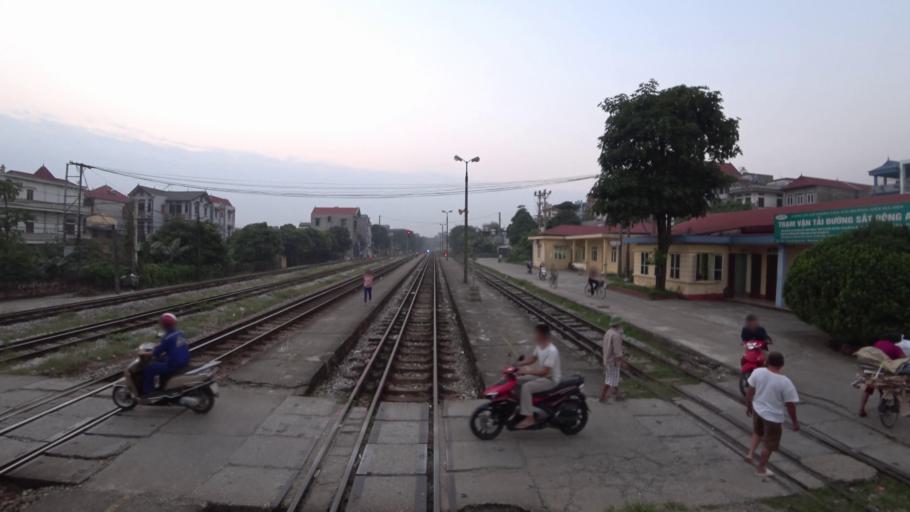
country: VN
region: Ha Noi
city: Soc Son
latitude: 21.2084
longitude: 105.8567
